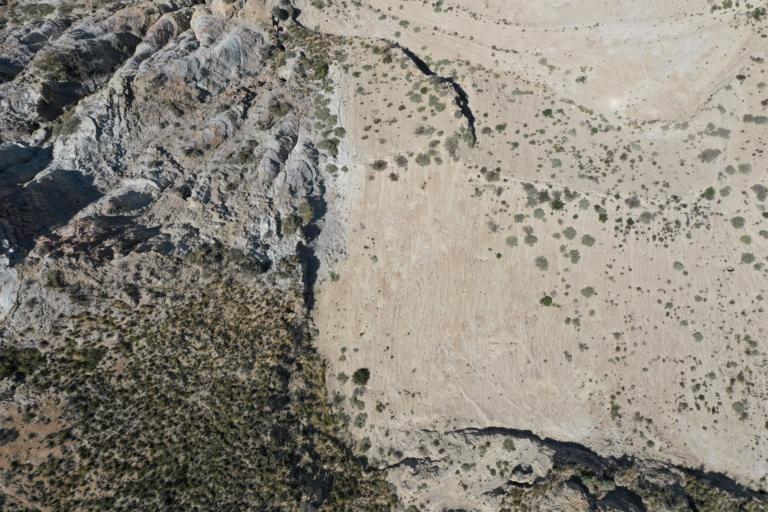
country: BO
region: La Paz
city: La Paz
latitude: -16.5548
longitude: -68.1231
